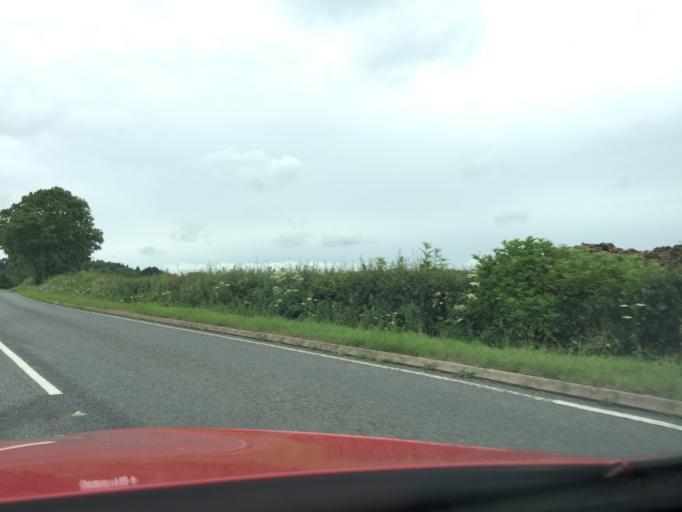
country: GB
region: England
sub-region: Warwickshire
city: Dunchurch
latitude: 52.2534
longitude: -1.2593
